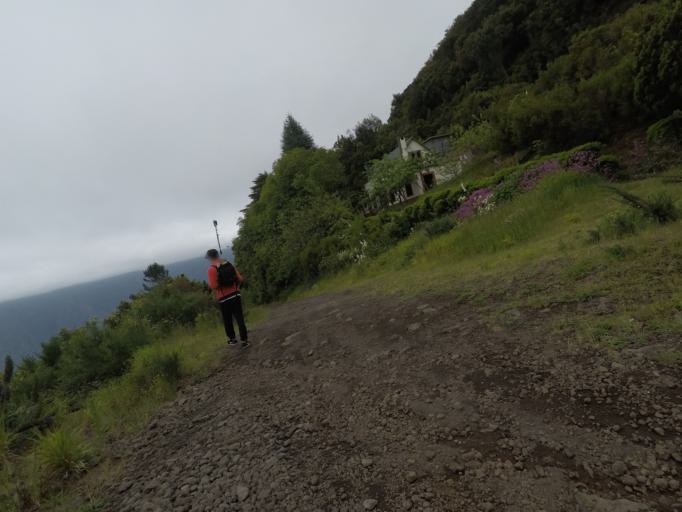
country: PT
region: Madeira
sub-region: Sao Vicente
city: Sao Vicente
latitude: 32.7742
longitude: -17.0558
